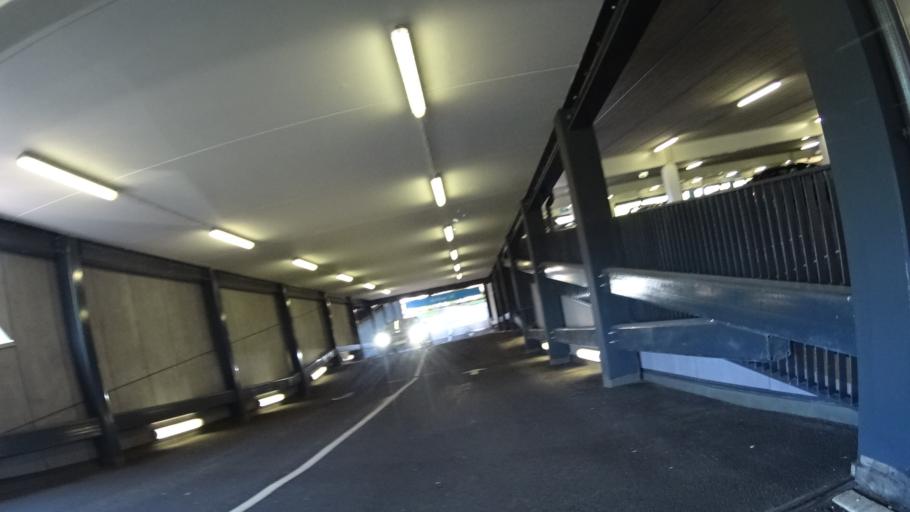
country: NL
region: South Holland
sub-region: Gemeente Delft
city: Delft
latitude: 52.0141
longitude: 4.3423
